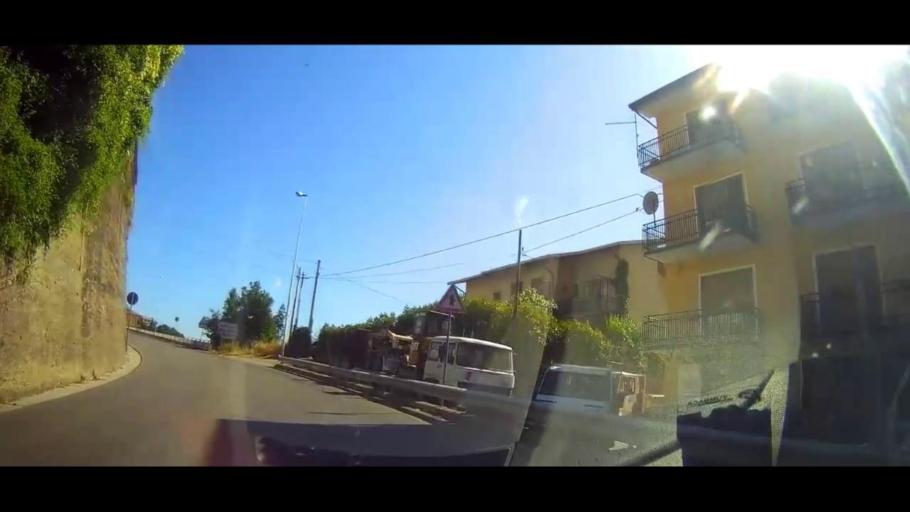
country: IT
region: Calabria
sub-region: Provincia di Cosenza
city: Celico
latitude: 39.3074
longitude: 16.3412
